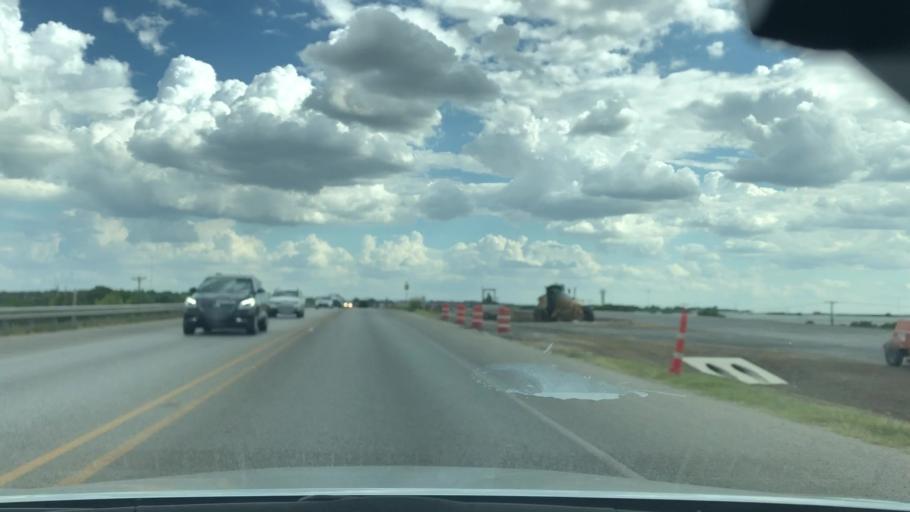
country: US
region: Texas
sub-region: Comal County
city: New Braunfels
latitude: 29.6837
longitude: -98.1552
